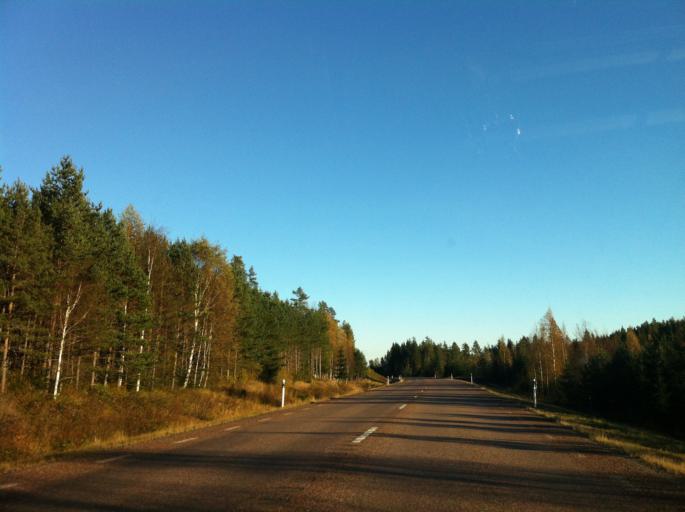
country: SE
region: Dalarna
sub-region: Faluns Kommun
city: Bjursas
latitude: 60.7490
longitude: 15.3559
